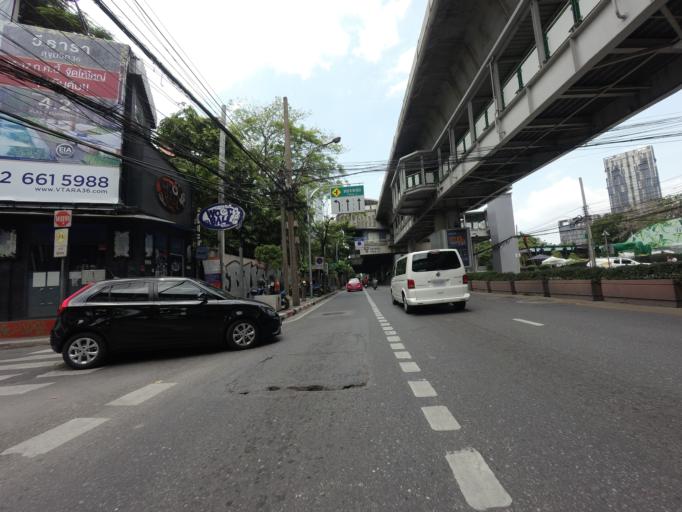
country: TH
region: Bangkok
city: Watthana
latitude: 13.7252
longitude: 100.5773
